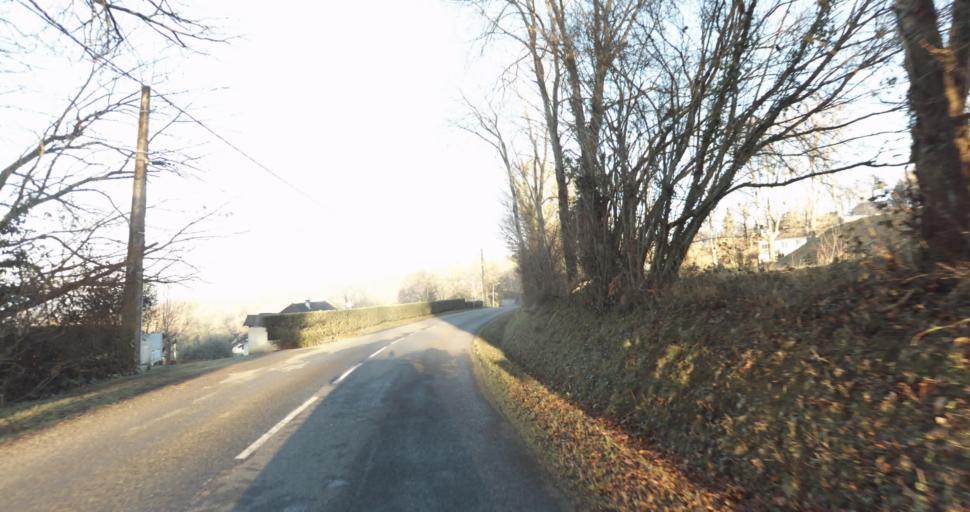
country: FR
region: Aquitaine
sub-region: Departement des Pyrenees-Atlantiques
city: Morlaas
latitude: 43.3284
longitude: -0.2689
